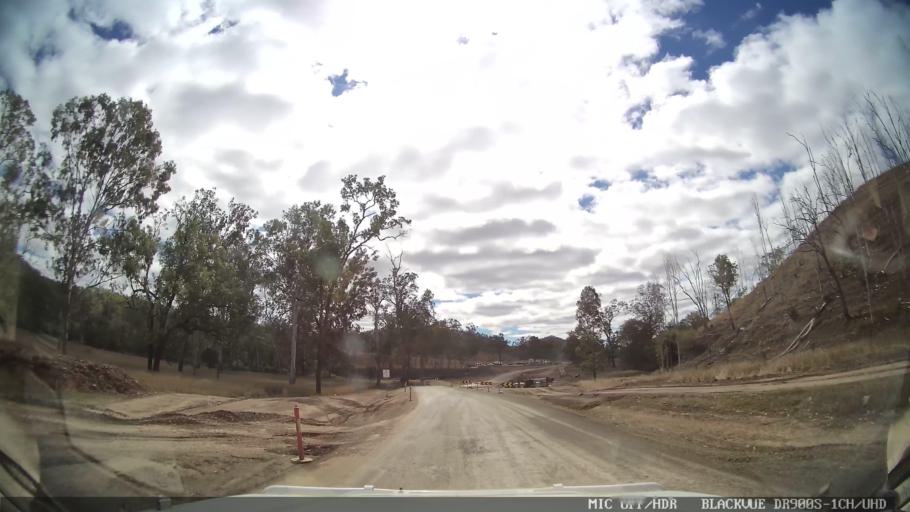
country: AU
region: Queensland
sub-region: Gladstone
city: Toolooa
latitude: -24.6157
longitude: 151.2989
